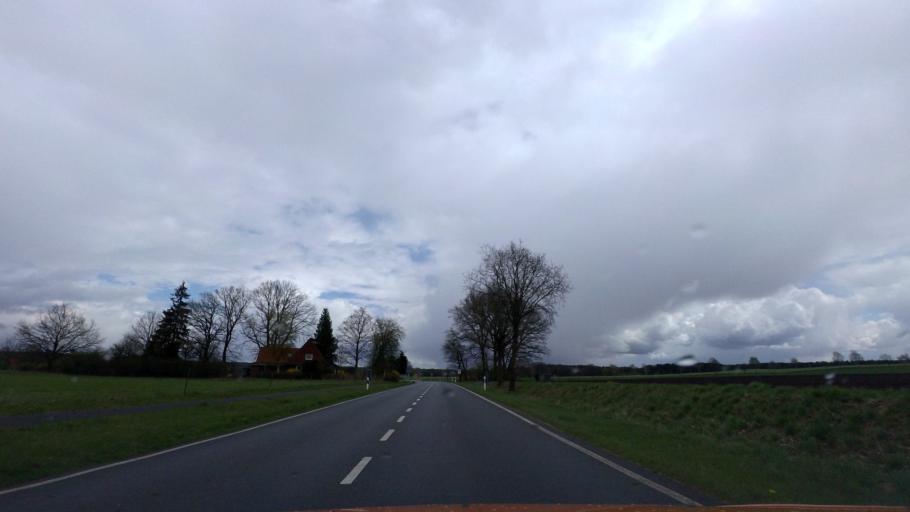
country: DE
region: Lower Saxony
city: Egestorf
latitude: 53.1450
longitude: 10.0521
